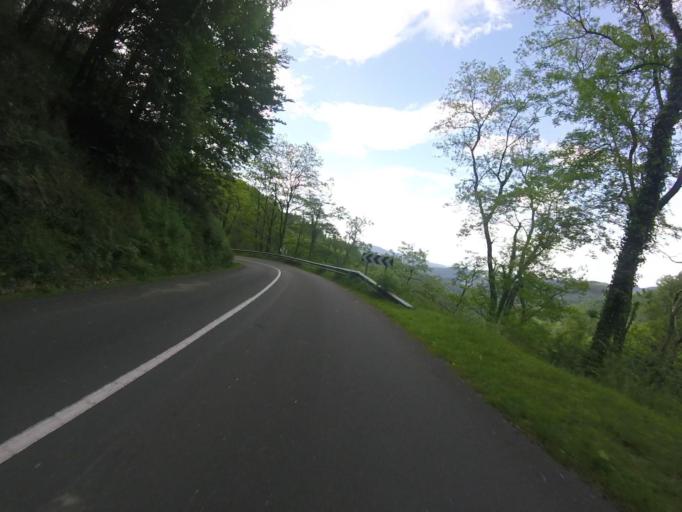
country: ES
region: Navarre
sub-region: Provincia de Navarra
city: Arano
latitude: 43.2523
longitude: -1.8491
